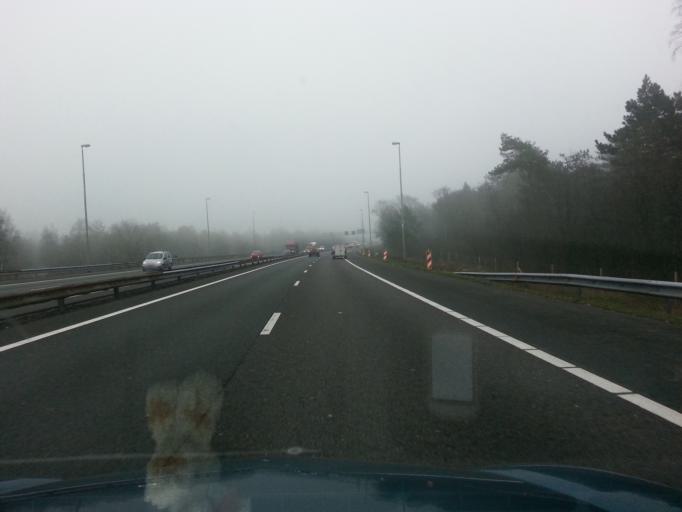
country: NL
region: Gelderland
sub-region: Gemeente Renkum
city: Renkum
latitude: 52.0223
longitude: 5.7269
